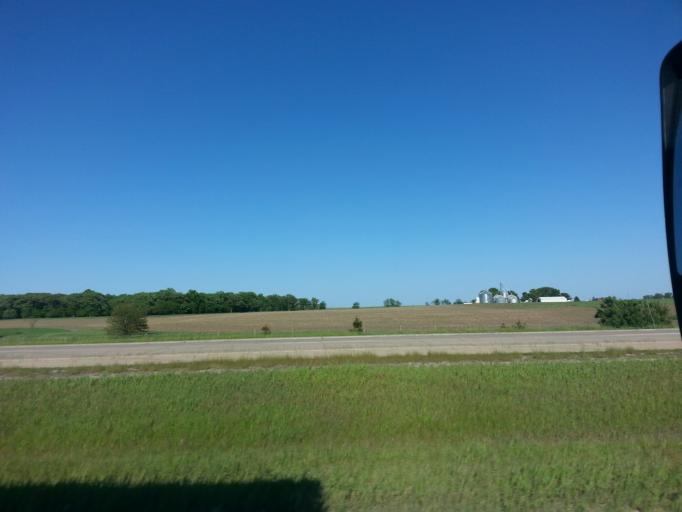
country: US
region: Illinois
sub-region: LaSalle County
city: Oglesby
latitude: 41.2002
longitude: -89.0770
